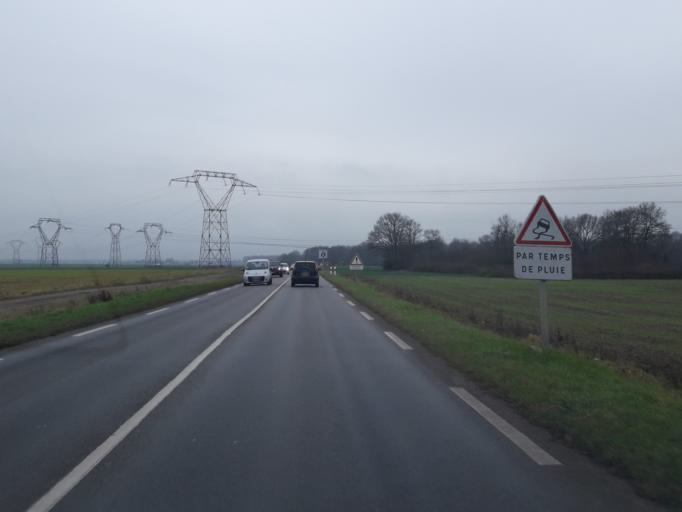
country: FR
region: Ile-de-France
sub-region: Departement de l'Essonne
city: Le Coudray-Montceaux
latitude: 48.5503
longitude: 2.4865
